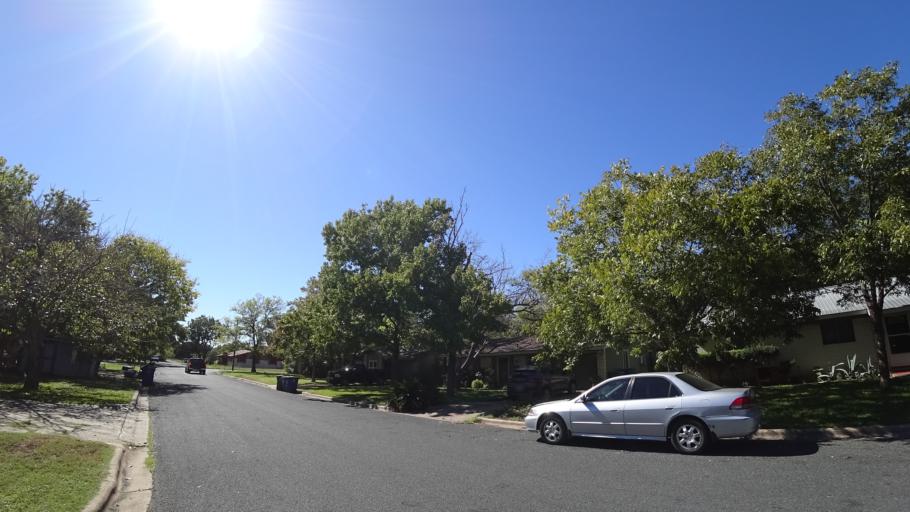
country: US
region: Texas
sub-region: Travis County
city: Rollingwood
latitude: 30.2187
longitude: -97.7872
